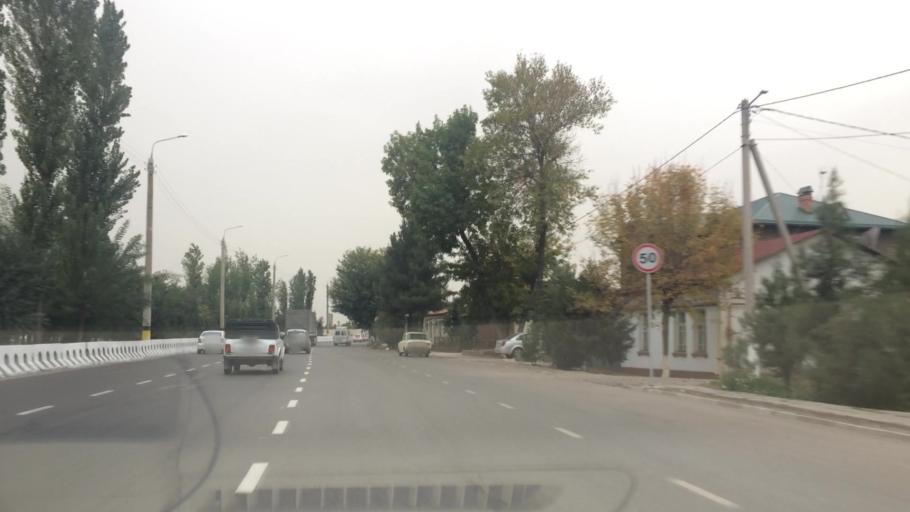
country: UZ
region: Toshkent
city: Salor
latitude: 41.3082
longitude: 69.3422
